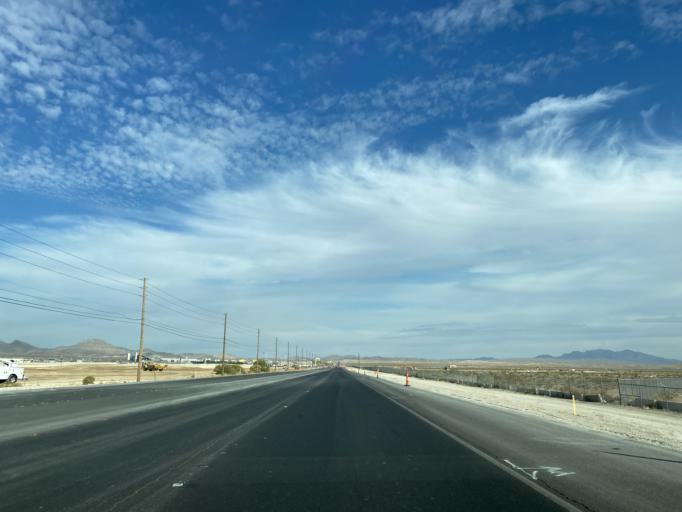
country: US
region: Nevada
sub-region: Clark County
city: Nellis Air Force Base
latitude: 36.2548
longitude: -115.0299
